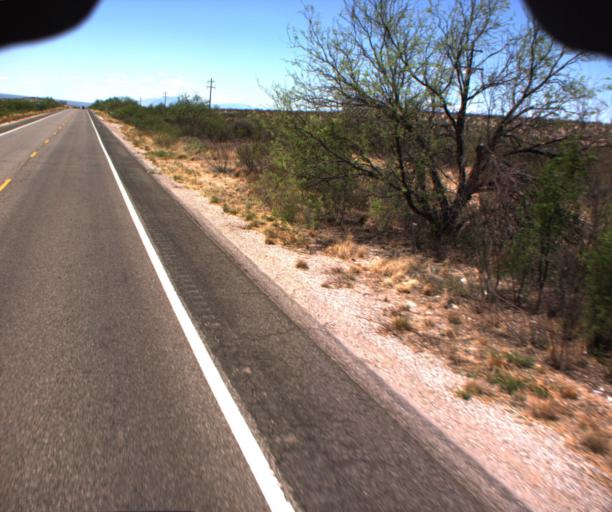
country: US
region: Arizona
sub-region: Cochise County
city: Tombstone
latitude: 31.7778
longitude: -110.1341
